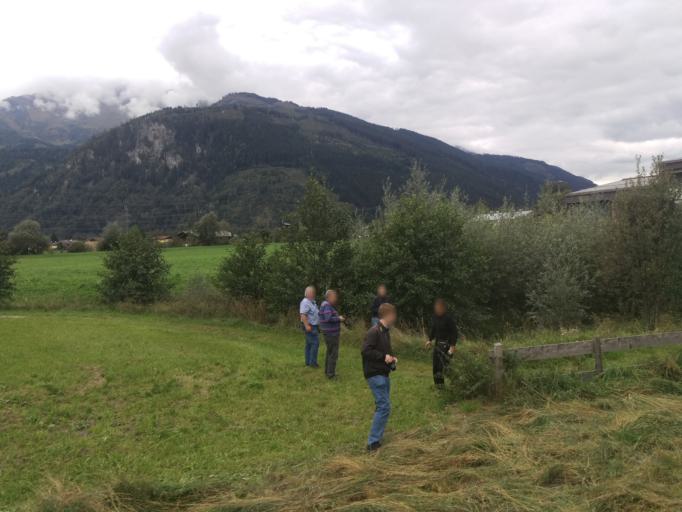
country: AT
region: Salzburg
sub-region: Politischer Bezirk Zell am See
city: Uttendorf
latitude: 47.2813
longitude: 12.5736
